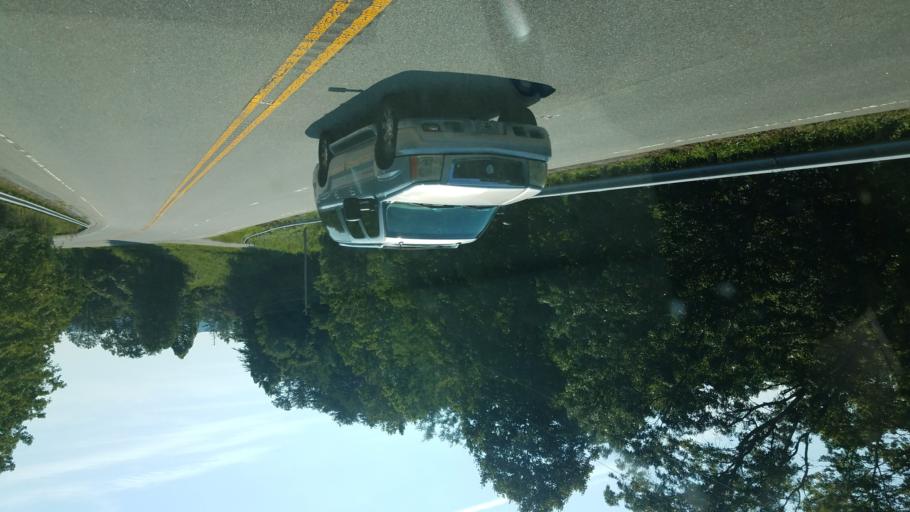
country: US
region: North Carolina
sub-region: Burke County
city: Glen Alpine
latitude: 35.9175
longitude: -81.8121
